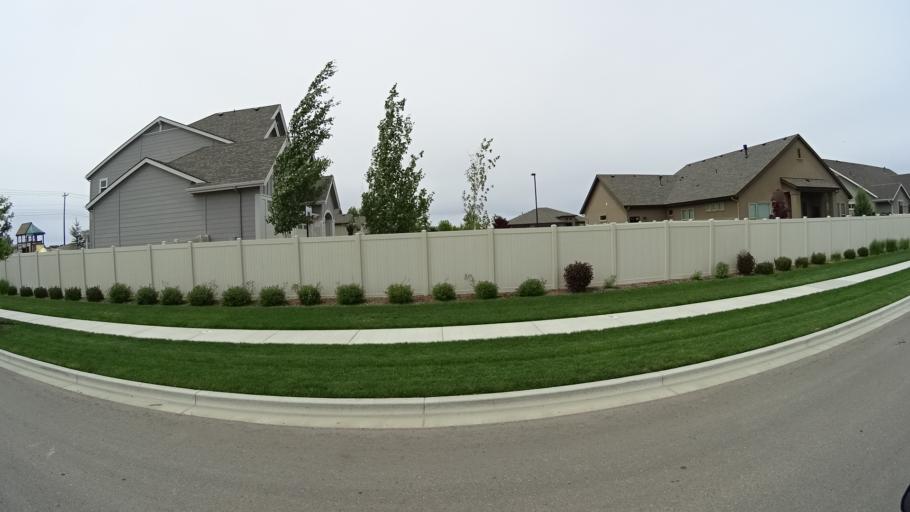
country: US
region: Idaho
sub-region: Ada County
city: Meridian
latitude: 43.5617
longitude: -116.3596
